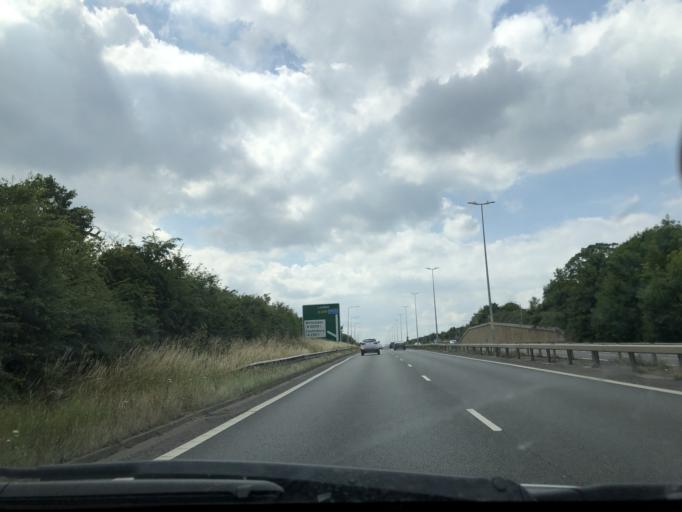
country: GB
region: England
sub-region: Kent
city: Whitstable
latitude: 51.3395
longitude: 1.0308
